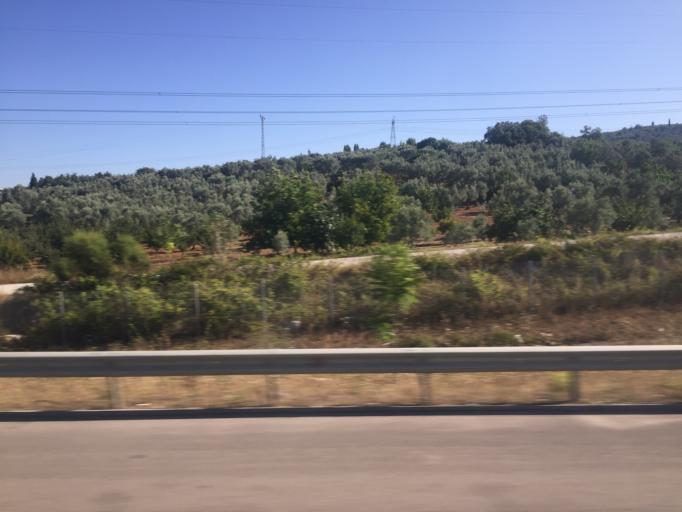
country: TR
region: Bursa
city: Demirtas
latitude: 40.2849
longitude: 29.0783
